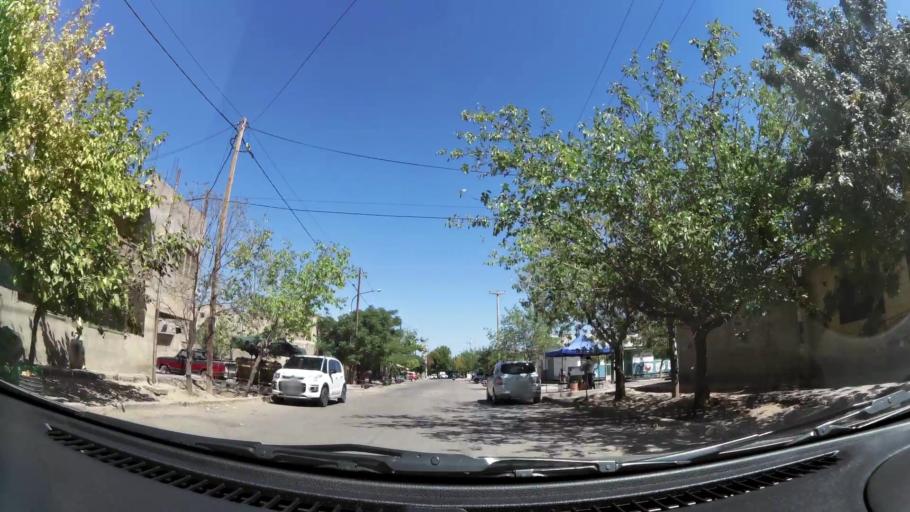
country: AR
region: Mendoza
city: Villa Nueva
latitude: -32.8799
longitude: -68.7981
